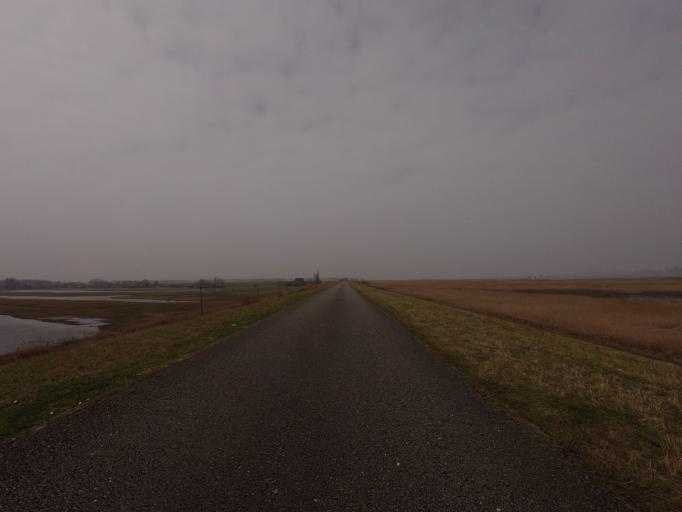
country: NL
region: North Brabant
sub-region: Gemeente Woensdrecht
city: Woensdrecht
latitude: 51.3344
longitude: 4.2500
